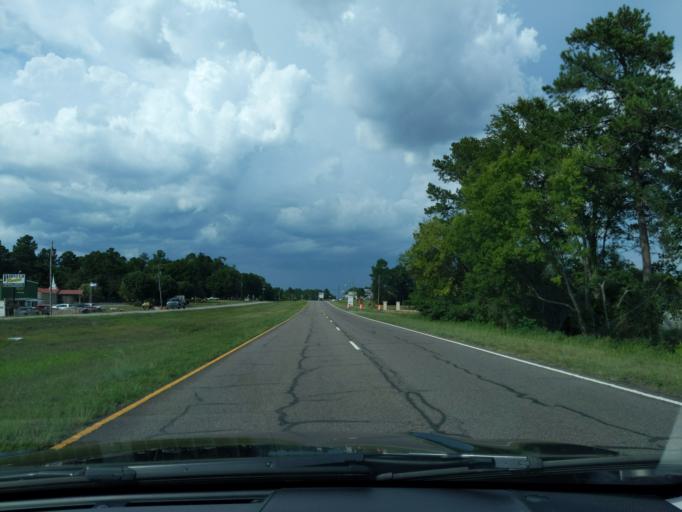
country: US
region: South Carolina
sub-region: Edgefield County
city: Murphys Estates
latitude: 33.6109
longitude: -81.9313
